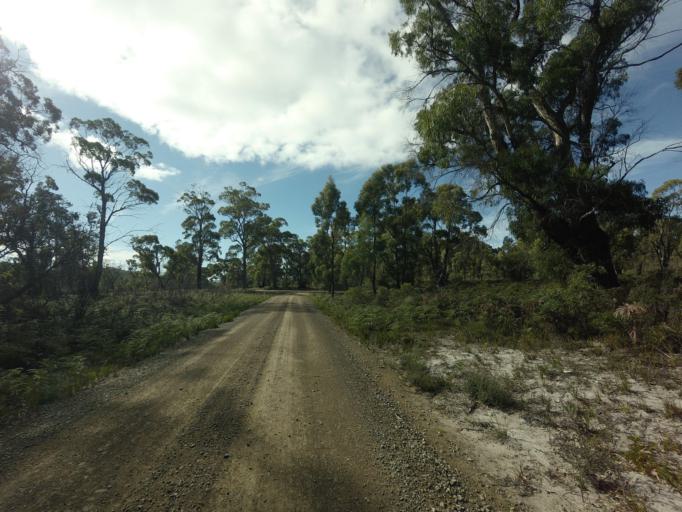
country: AU
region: Tasmania
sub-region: Clarence
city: Sandford
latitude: -42.9800
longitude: 147.7135
